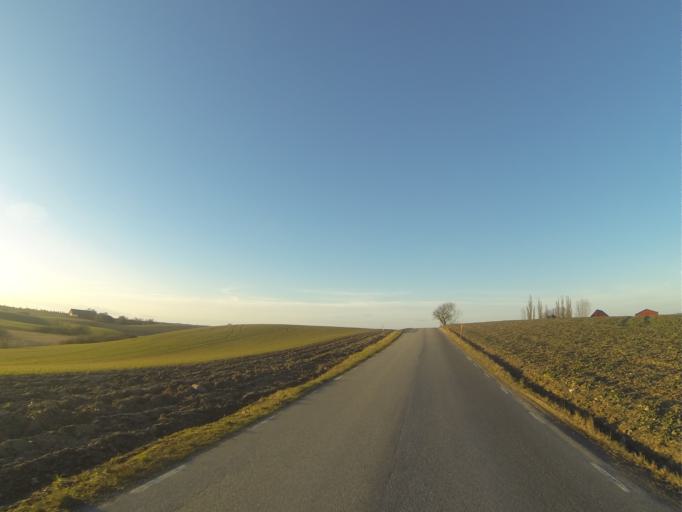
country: SE
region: Skane
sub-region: Staffanstorps Kommun
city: Staffanstorp
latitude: 55.5954
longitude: 13.1798
